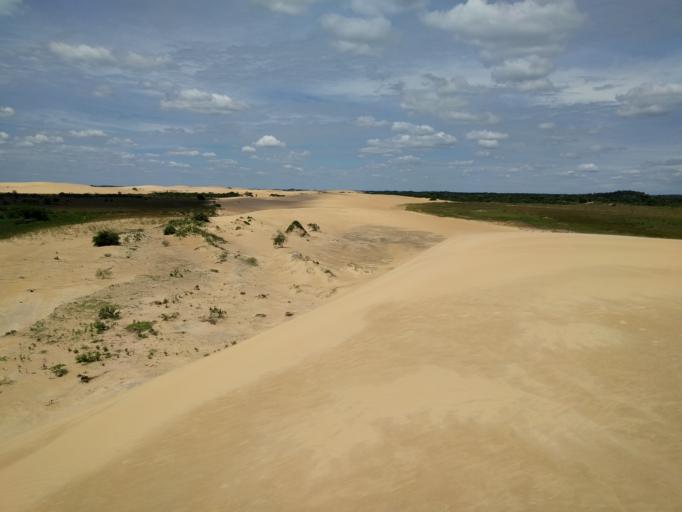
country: BO
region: Santa Cruz
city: Santa Cruz de la Sierra
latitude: -17.9450
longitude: -63.1599
